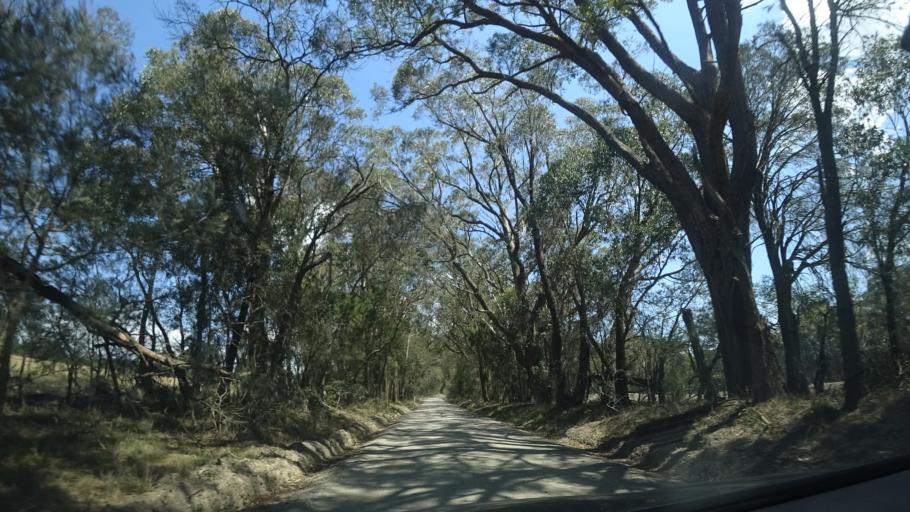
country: AU
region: New South Wales
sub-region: Wingecarribee
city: Bundanoon
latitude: -34.6315
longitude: 150.2585
